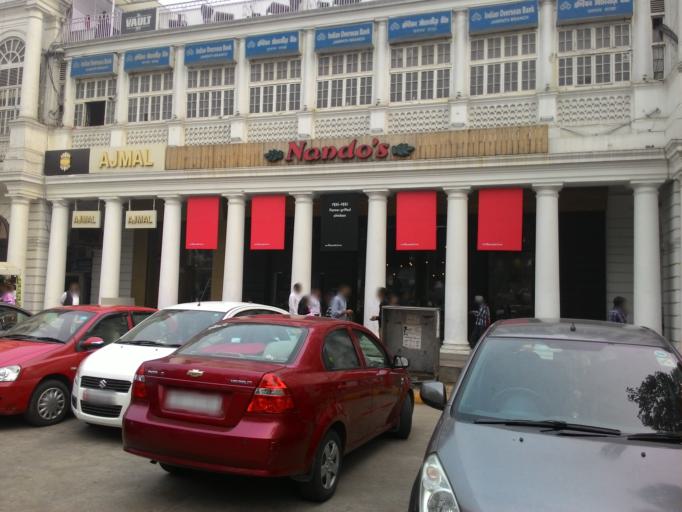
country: IN
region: NCT
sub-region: New Delhi
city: New Delhi
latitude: 28.6308
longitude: 77.2198
